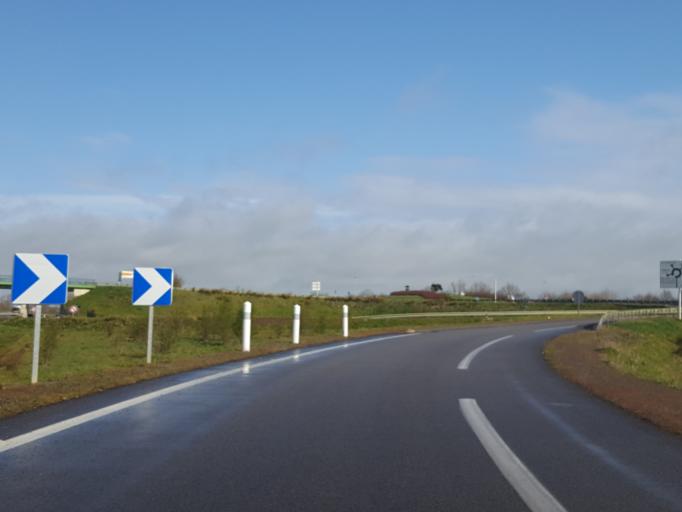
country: FR
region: Pays de la Loire
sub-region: Departement de la Vendee
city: Saligny
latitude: 46.7964
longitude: -1.4293
